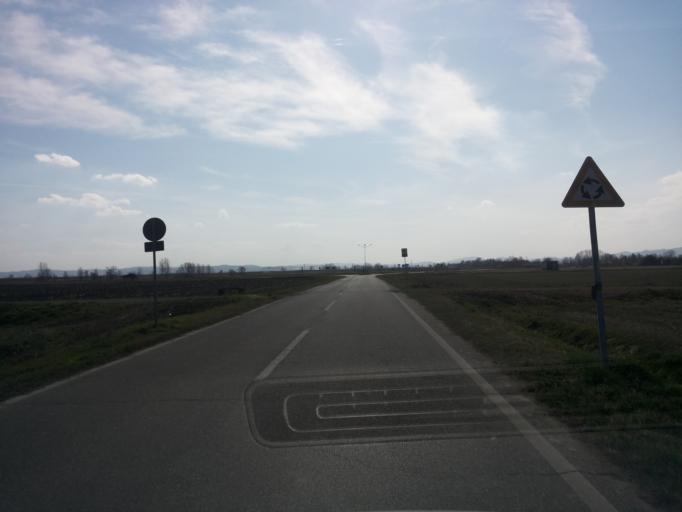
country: IT
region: Piedmont
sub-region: Provincia di Vercelli
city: Costanzana
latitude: 45.2377
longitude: 8.3780
